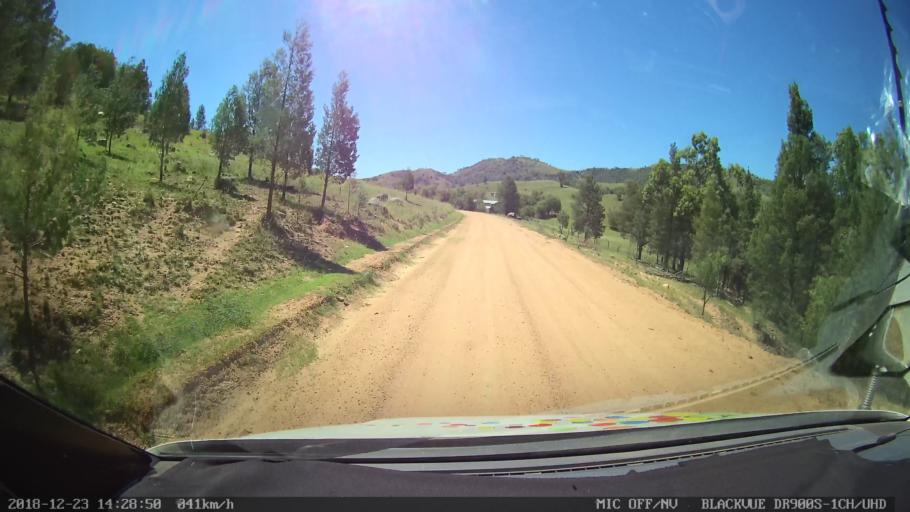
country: AU
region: New South Wales
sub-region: Tamworth Municipality
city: Manilla
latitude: -30.6122
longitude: 150.9400
